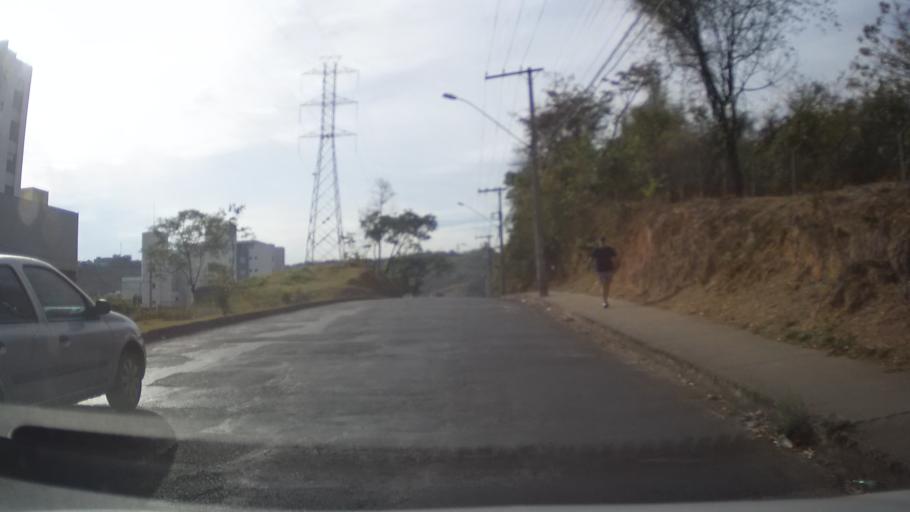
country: BR
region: Minas Gerais
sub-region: Belo Horizonte
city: Belo Horizonte
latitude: -19.8828
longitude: -43.9989
